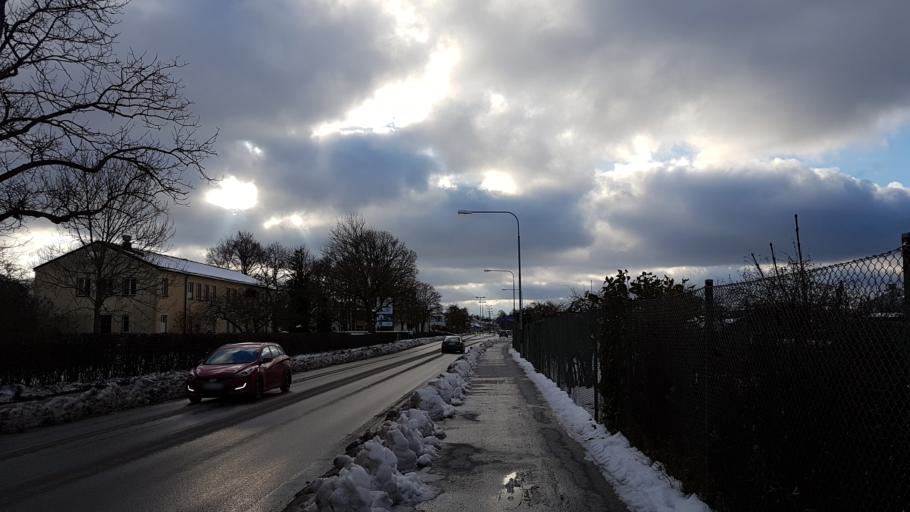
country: SE
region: Gotland
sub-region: Gotland
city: Visby
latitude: 57.6397
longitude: 18.3068
